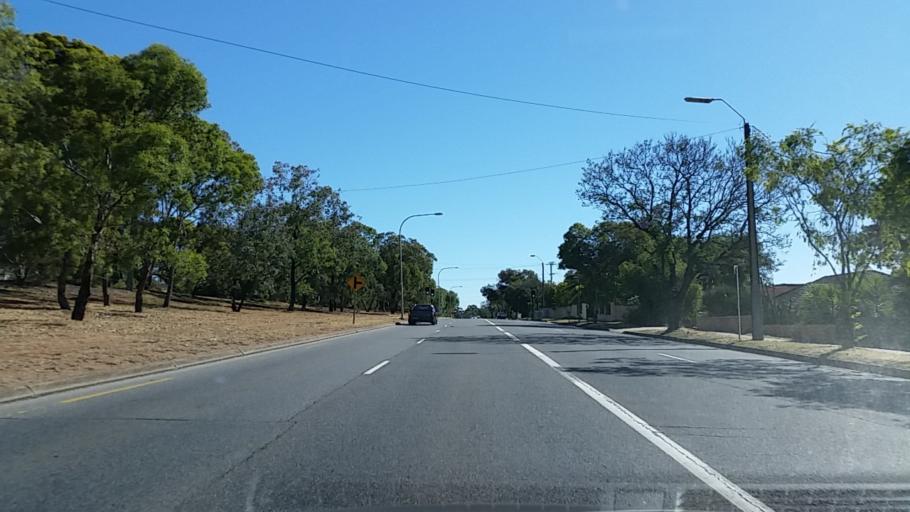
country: AU
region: South Australia
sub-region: Salisbury
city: Ingle Farm
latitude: -34.8315
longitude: 138.6292
